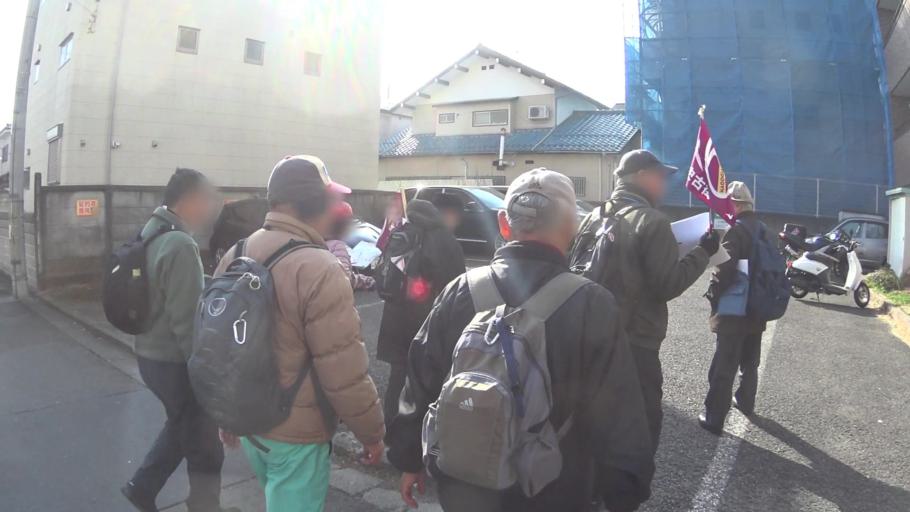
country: JP
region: Tokyo
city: Kokubunji
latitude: 35.6675
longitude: 139.4951
